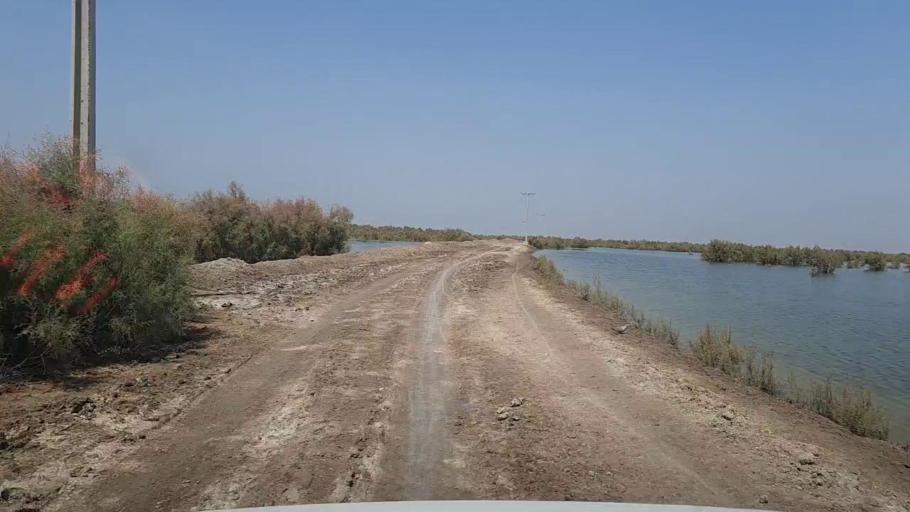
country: PK
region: Sindh
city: Kandhkot
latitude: 28.3461
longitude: 69.3016
